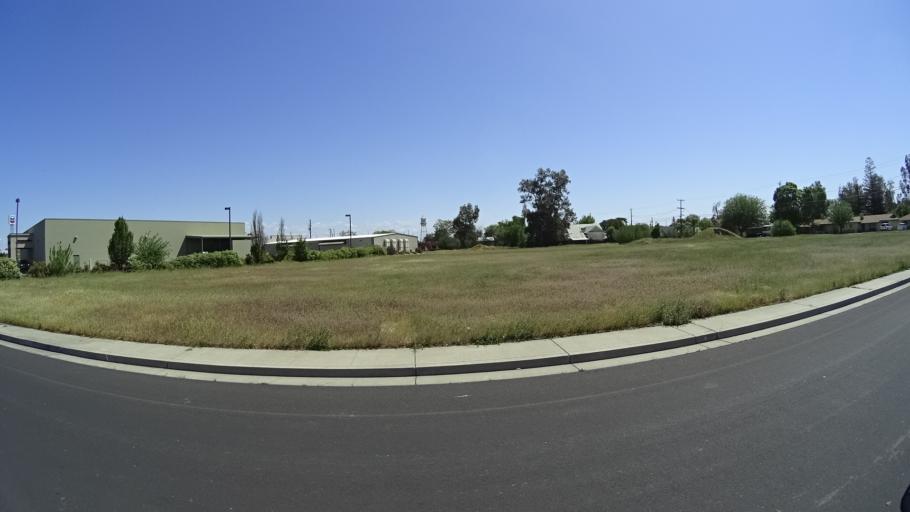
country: US
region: California
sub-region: Glenn County
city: Orland
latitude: 39.7481
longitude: -122.2028
